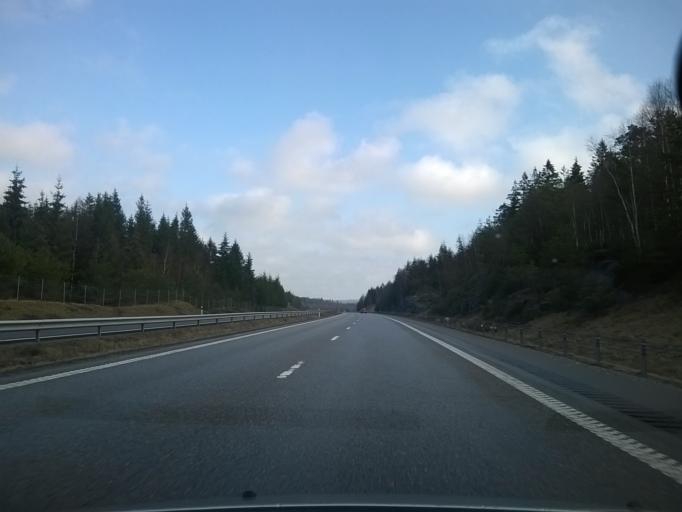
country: SE
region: Vaestra Goetaland
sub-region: Uddevalla Kommun
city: Ljungskile
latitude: 58.1819
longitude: 11.9075
